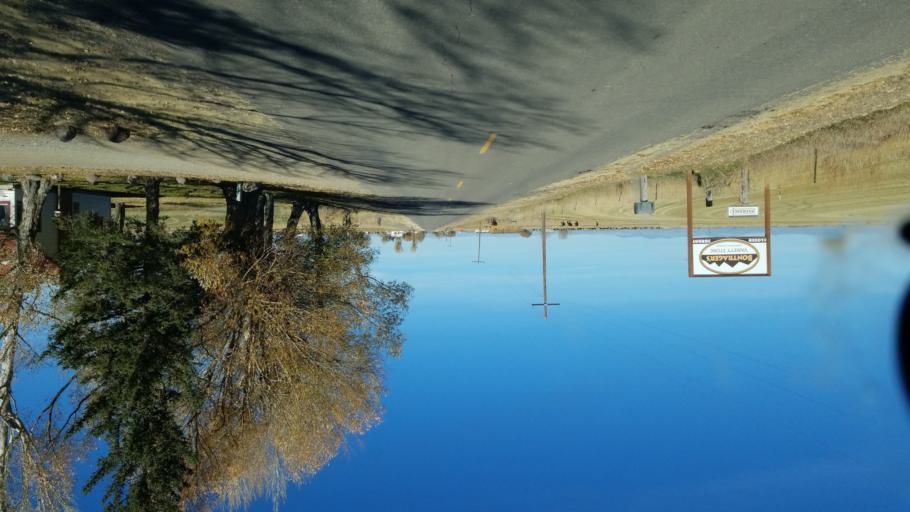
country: US
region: Colorado
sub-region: Rio Grande County
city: Monte Vista
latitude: 37.4336
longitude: -106.0942
